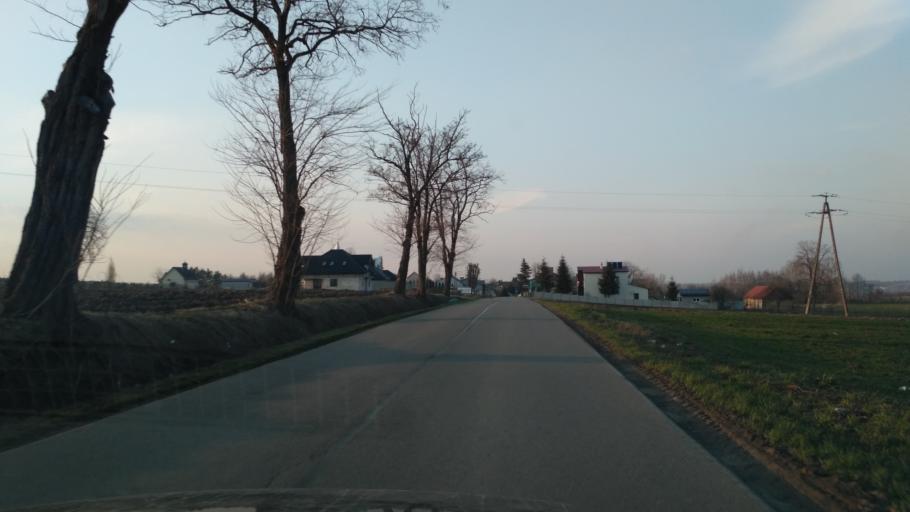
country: PL
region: Subcarpathian Voivodeship
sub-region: Powiat przeworski
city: Zarzecze
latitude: 49.9599
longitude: 22.5573
